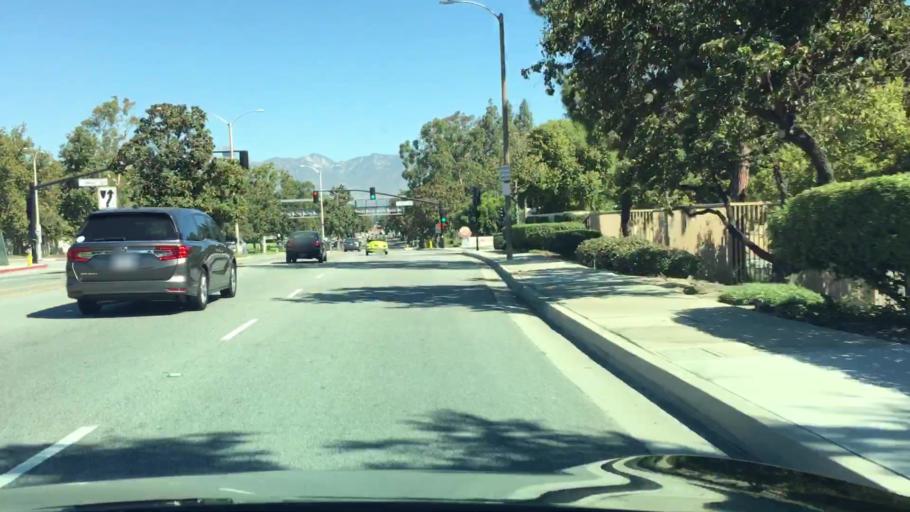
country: US
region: California
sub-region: Los Angeles County
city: South San Gabriel
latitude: 34.0510
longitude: -118.0818
